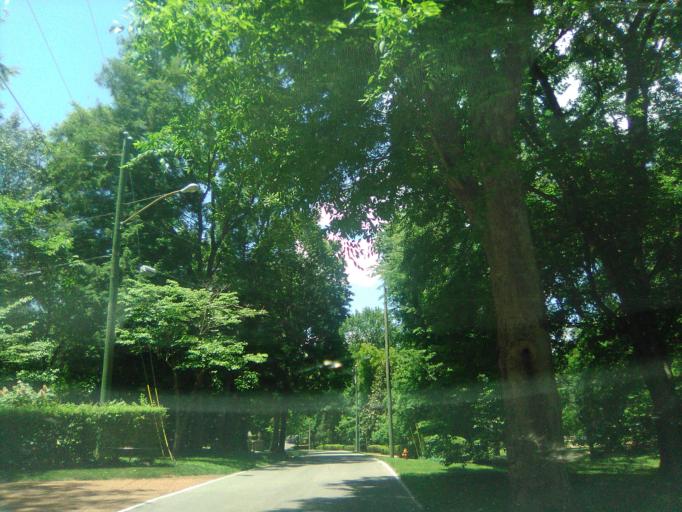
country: US
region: Tennessee
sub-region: Davidson County
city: Belle Meade
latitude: 36.1143
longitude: -86.8589
